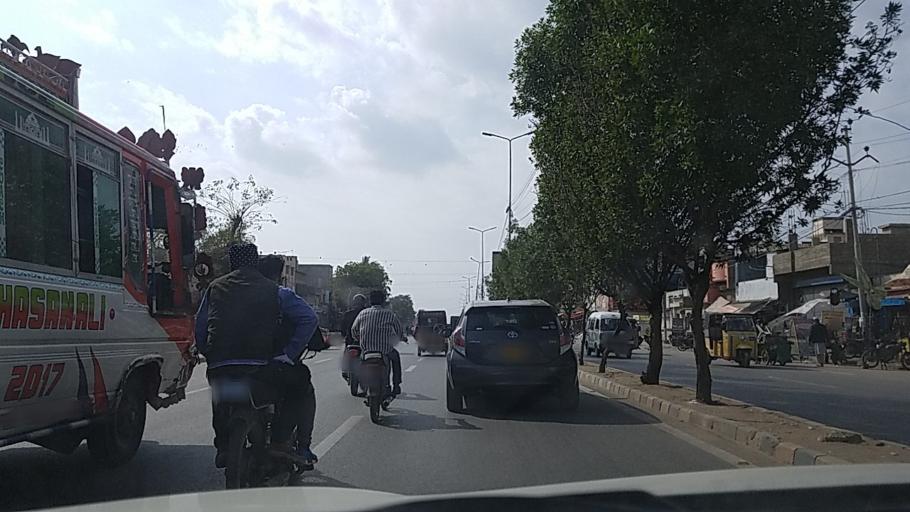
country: PK
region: Sindh
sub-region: Karachi District
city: Karachi
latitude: 24.8226
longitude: 67.1358
